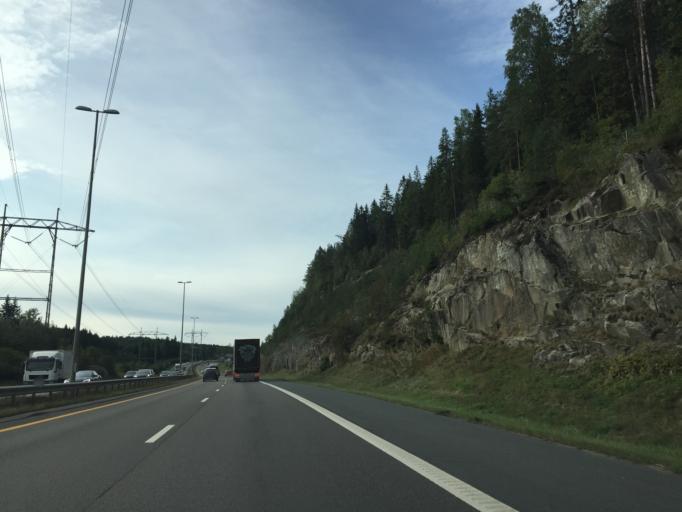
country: NO
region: Akershus
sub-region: Oppegard
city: Kolbotn
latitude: 59.8252
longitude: 10.8443
